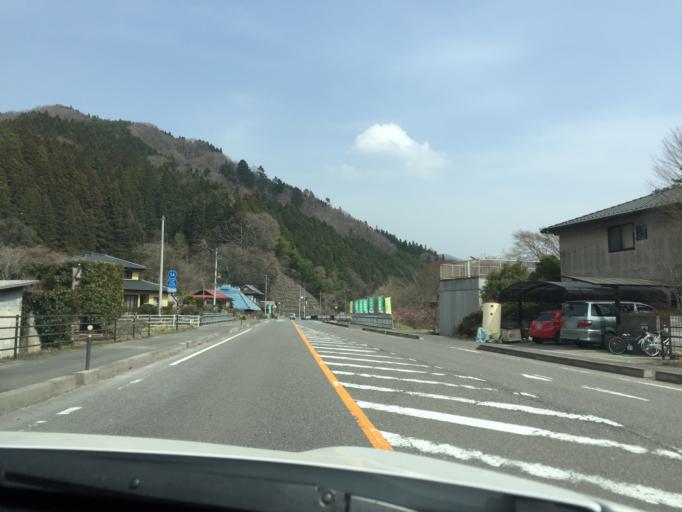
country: JP
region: Fukushima
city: Ishikawa
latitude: 37.0570
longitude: 140.5868
